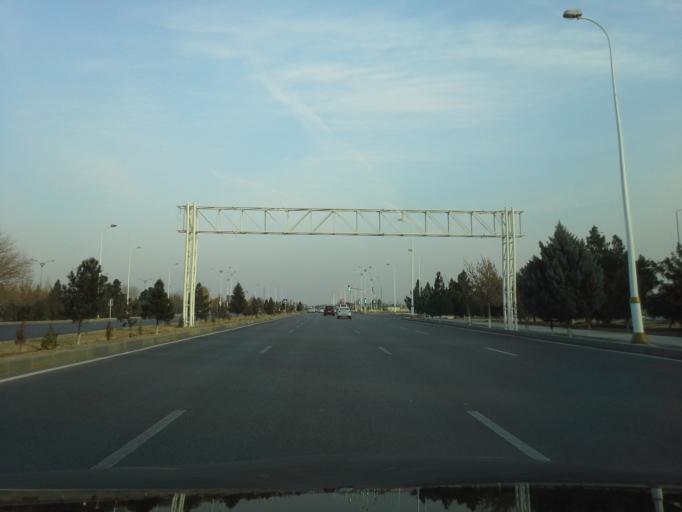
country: TM
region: Ahal
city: Abadan
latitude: 38.0348
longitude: 58.2221
